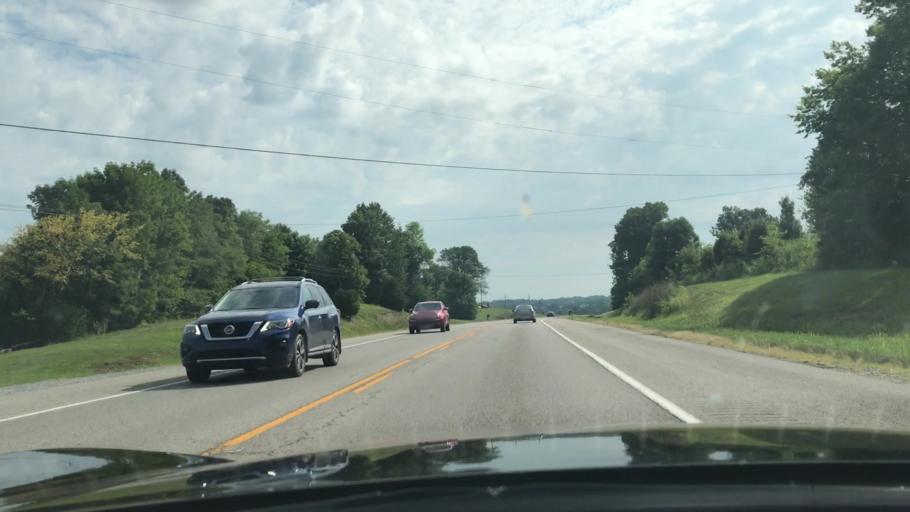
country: US
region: Kentucky
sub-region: Green County
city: Greensburg
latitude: 37.2890
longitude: -85.4785
